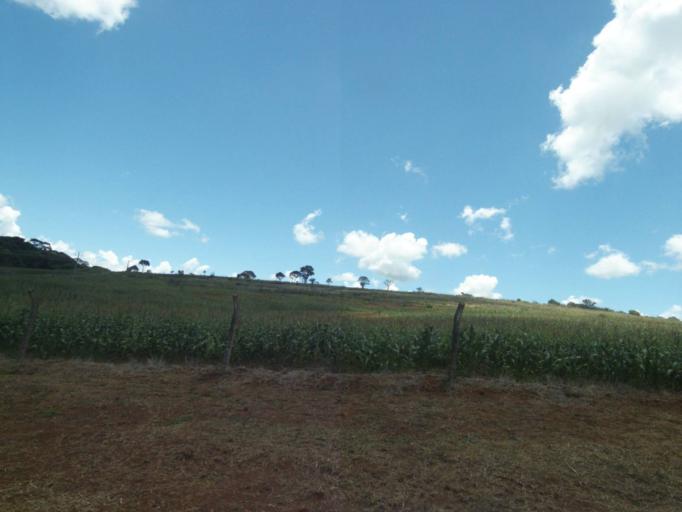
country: BR
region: Parana
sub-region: Pinhao
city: Pinhao
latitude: -25.7878
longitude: -52.0753
